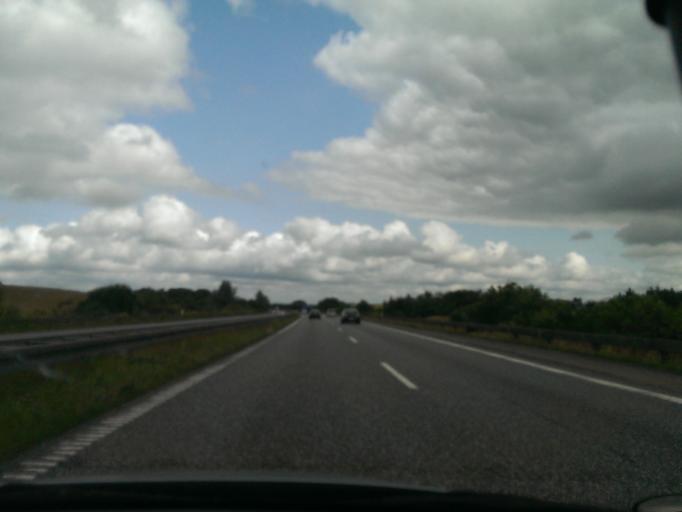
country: DK
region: North Denmark
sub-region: Mariagerfjord Kommune
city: Hobro
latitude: 56.6484
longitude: 9.7381
